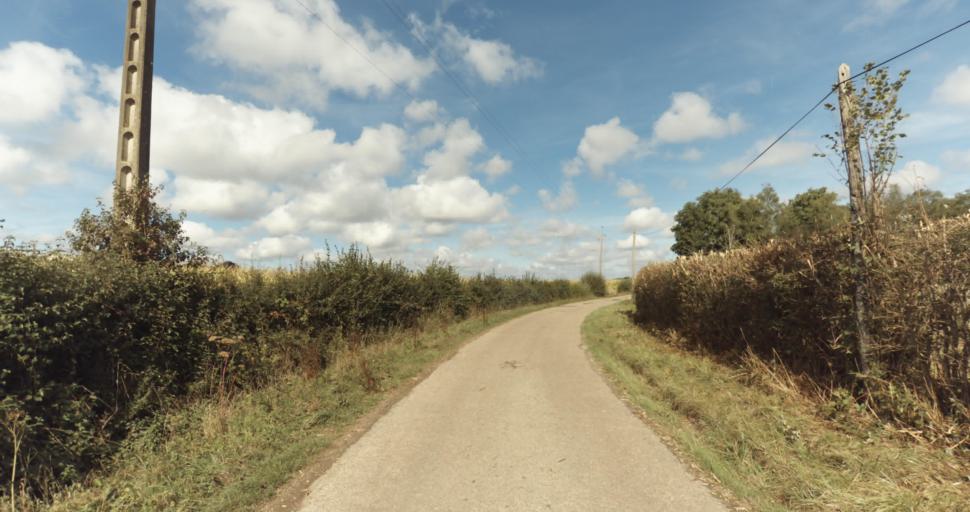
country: FR
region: Lower Normandy
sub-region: Departement du Calvados
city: La Vespiere
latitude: 48.9430
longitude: 0.3229
